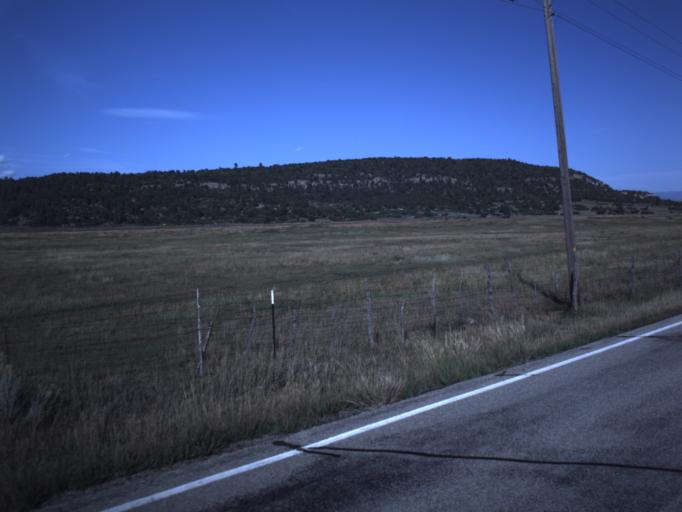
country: US
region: Utah
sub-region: Grand County
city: Moab
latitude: 38.3297
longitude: -109.1434
